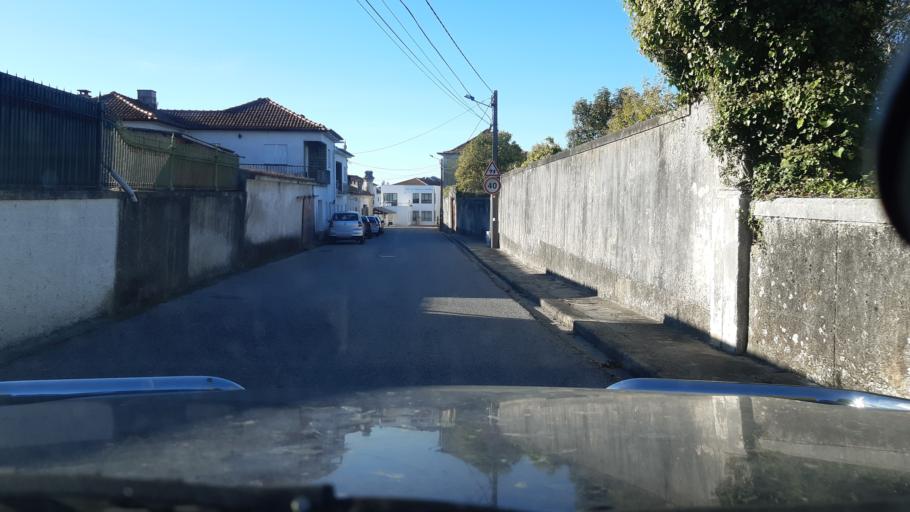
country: PT
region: Aveiro
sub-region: Agueda
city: Agueda
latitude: 40.5575
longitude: -8.4367
